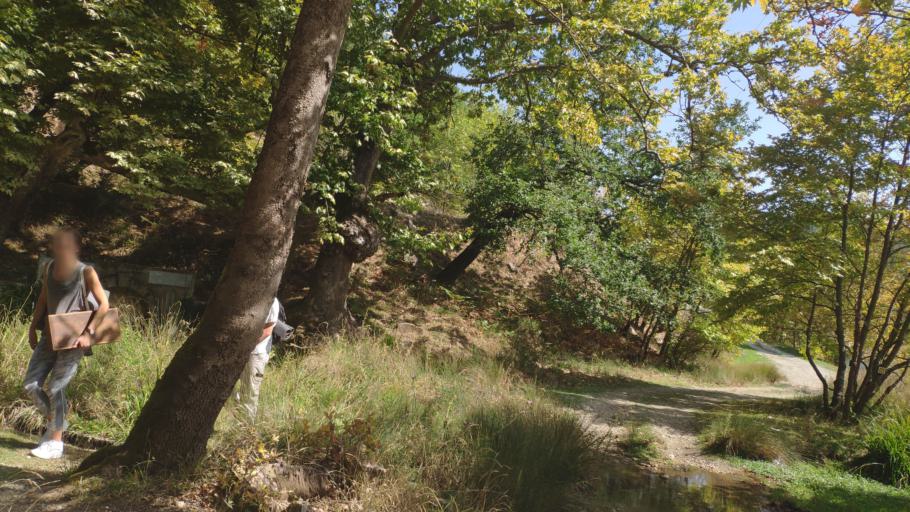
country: GR
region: West Greece
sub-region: Nomos Achaias
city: Kalavryta
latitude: 37.9314
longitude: 22.2843
